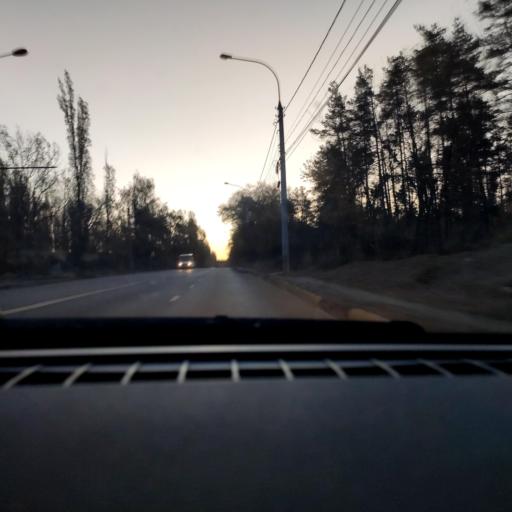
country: RU
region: Voronezj
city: Somovo
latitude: 51.7028
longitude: 39.2794
